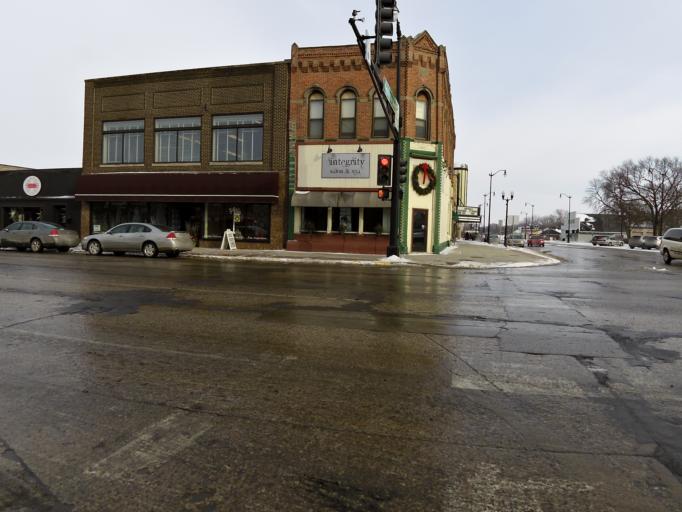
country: US
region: Minnesota
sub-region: McLeod County
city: Hutchinson
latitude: 44.8924
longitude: -94.3694
